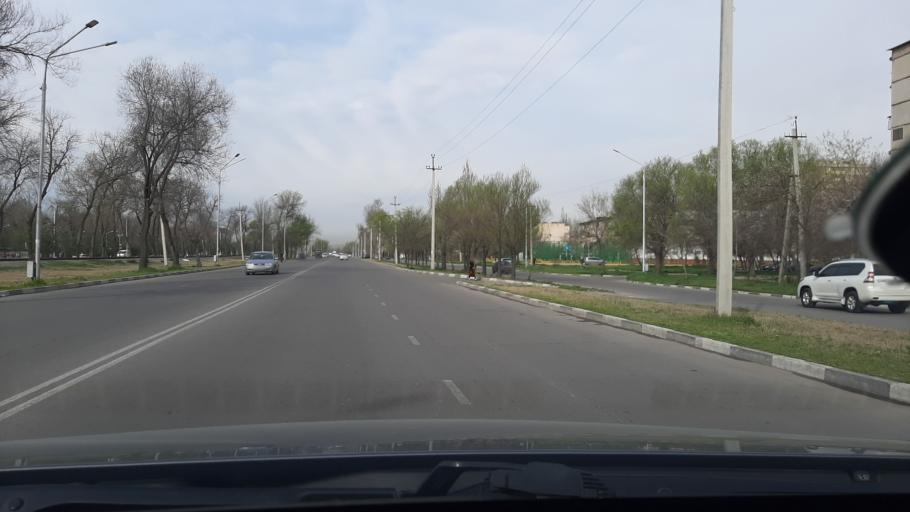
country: TJ
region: Dushanbe
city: Dushanbe
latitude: 38.5690
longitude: 68.7499
